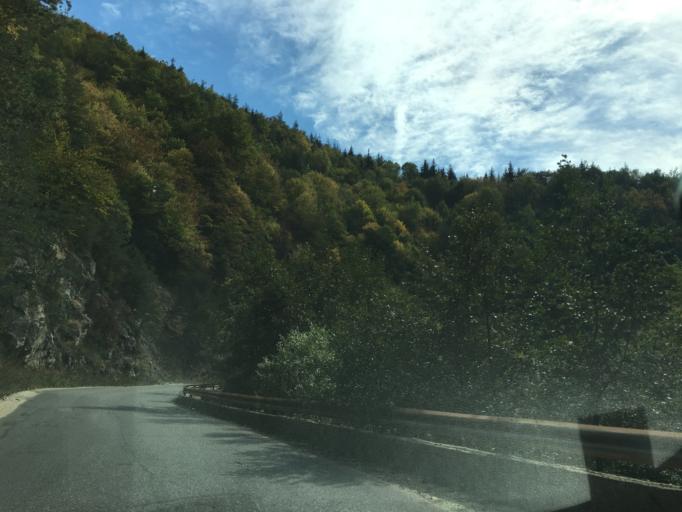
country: BG
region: Pazardzhik
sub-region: Obshtina Batak
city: Batak
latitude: 41.9593
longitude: 24.2389
